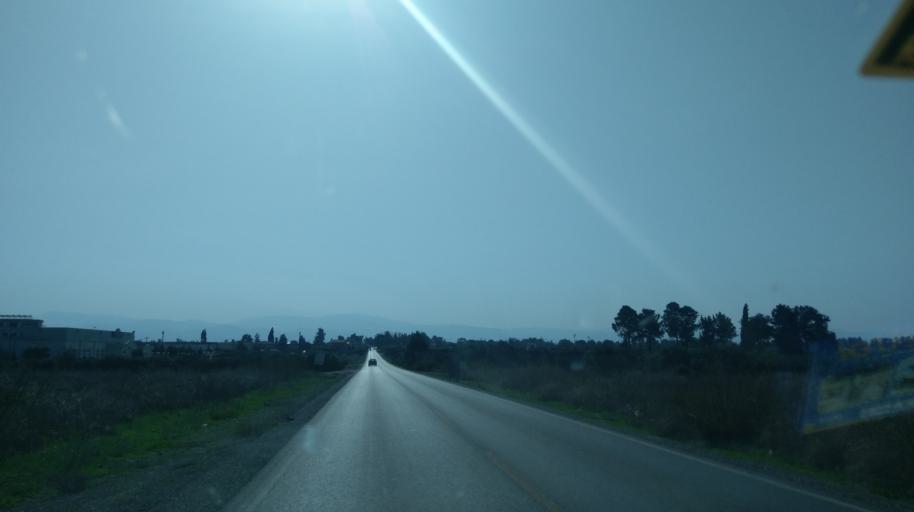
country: CY
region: Lefkosia
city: Morfou
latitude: 35.2142
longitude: 33.0036
